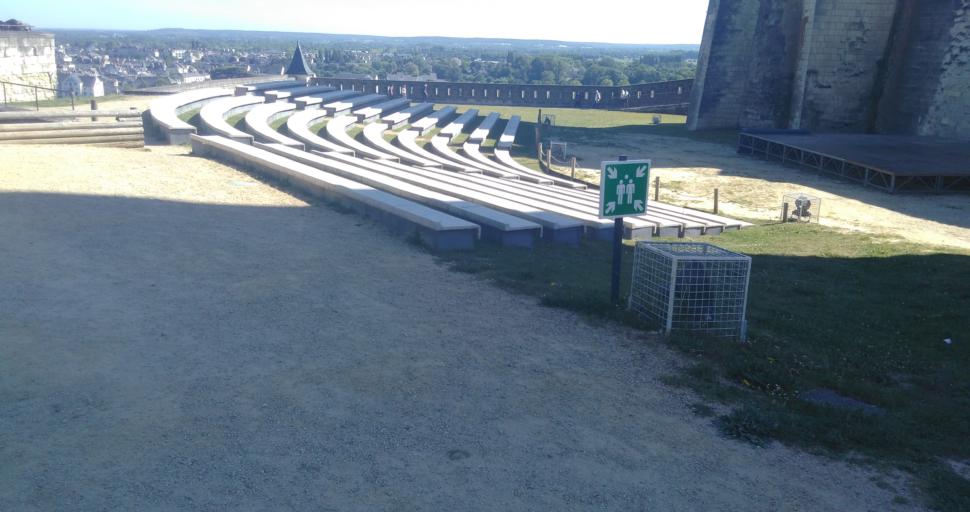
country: FR
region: Pays de la Loire
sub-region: Departement de Maine-et-Loire
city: Saumur
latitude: 47.2570
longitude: -0.0730
